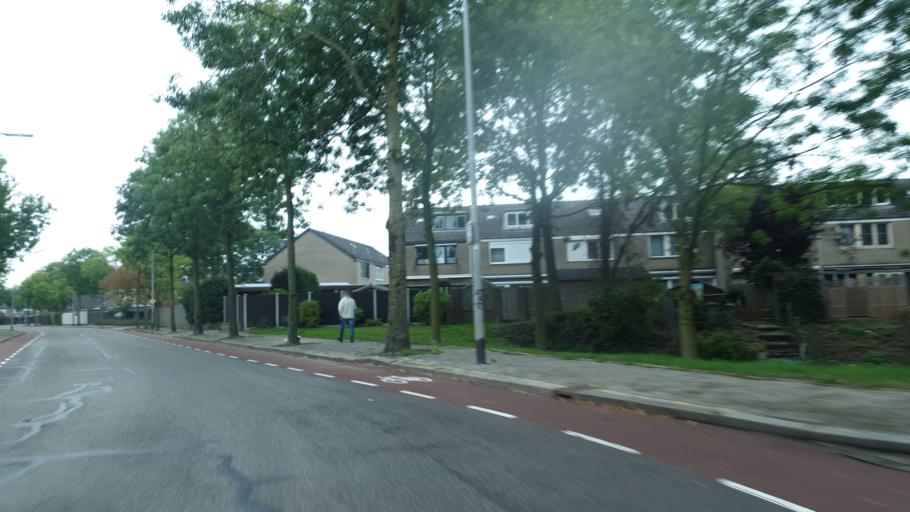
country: NL
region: Gelderland
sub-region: Gemeente Nijmegen
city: Lindenholt
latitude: 51.8189
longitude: 5.8075
